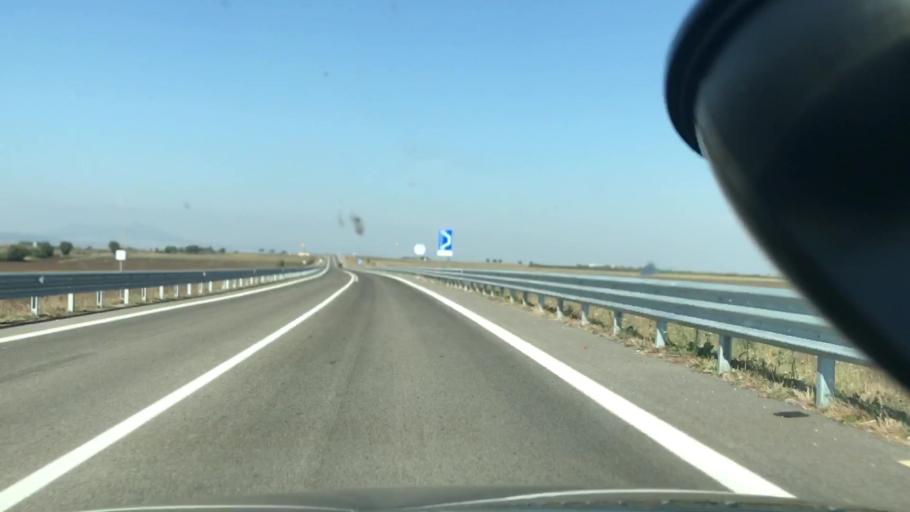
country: IT
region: Basilicate
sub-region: Provincia di Potenza
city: Palazzo San Gervasio
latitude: 40.9714
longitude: 15.9912
